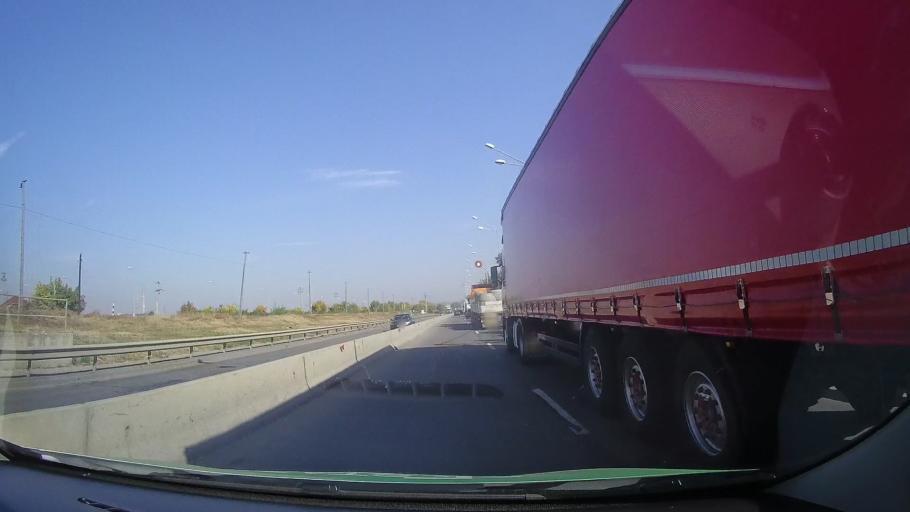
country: RO
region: Bihor
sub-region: Comuna Biharea
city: Oradea
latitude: 47.0638
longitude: 21.8974
